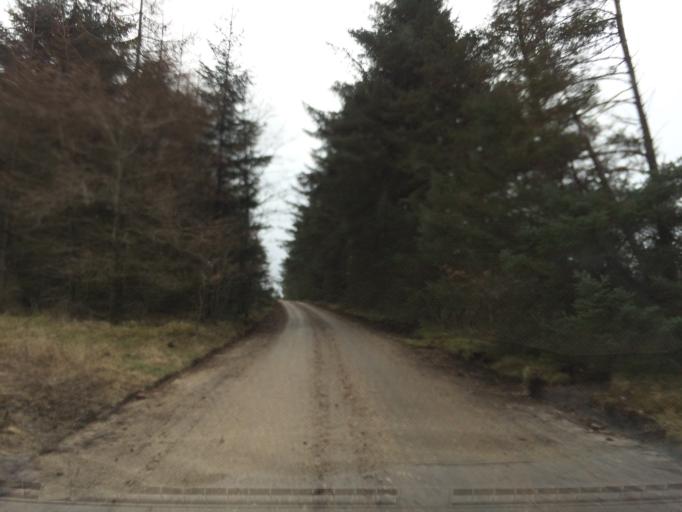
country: DK
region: Central Jutland
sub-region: Holstebro Kommune
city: Holstebro
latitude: 56.2253
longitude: 8.4970
